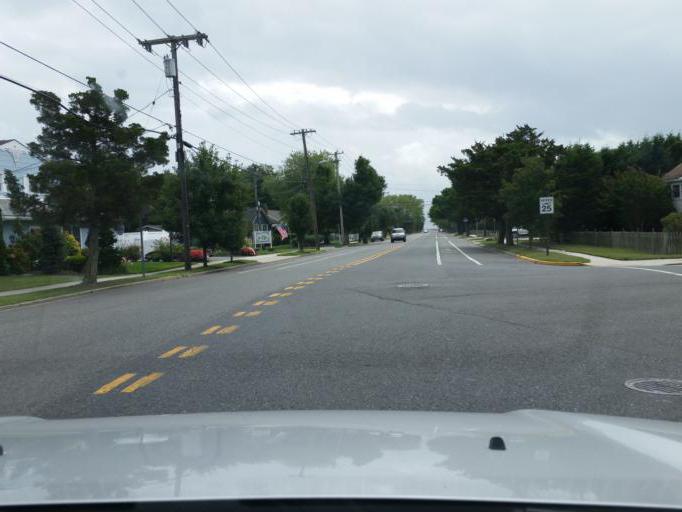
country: US
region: New Jersey
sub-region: Cape May County
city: Cape May
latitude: 38.9374
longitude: -74.9149
